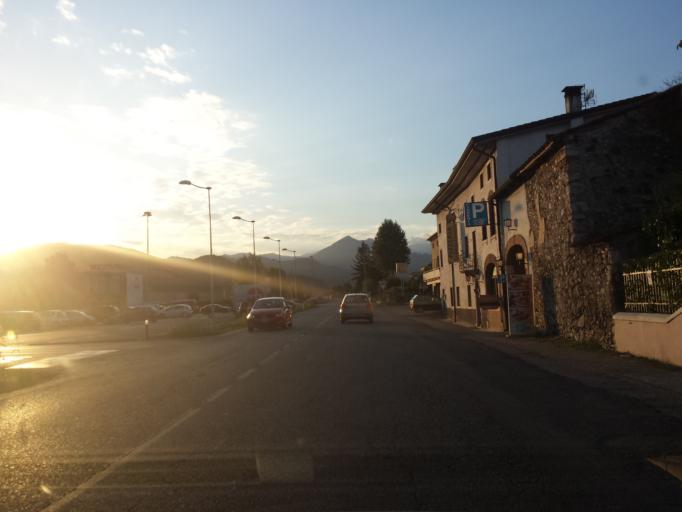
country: IT
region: Veneto
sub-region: Provincia di Vicenza
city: Cereda-Cozza Cornedo
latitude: 45.5996
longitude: 11.3639
